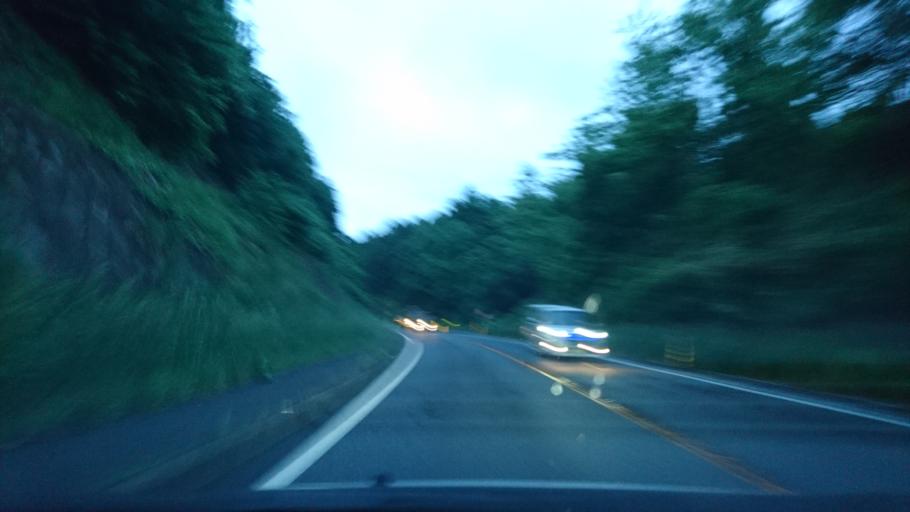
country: JP
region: Iwate
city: Ichinoseki
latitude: 38.8568
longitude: 141.0987
